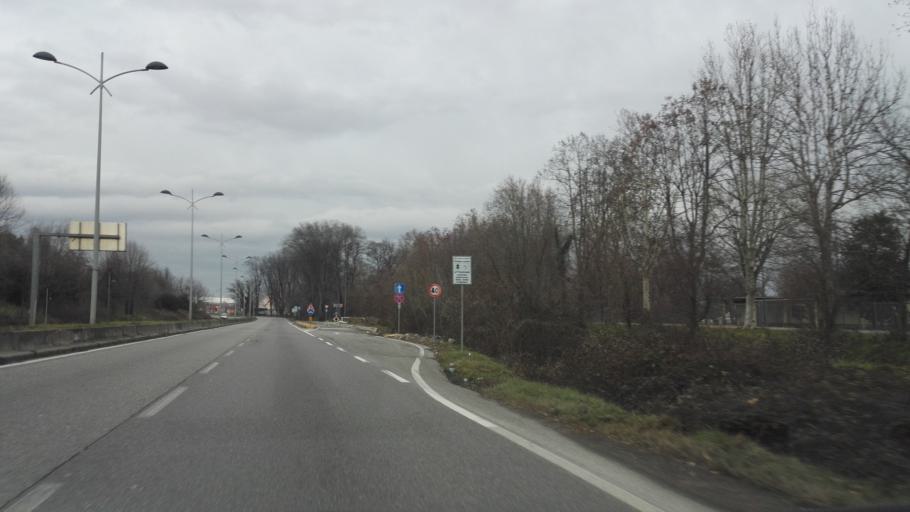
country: IT
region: Lombardy
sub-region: Citta metropolitana di Milano
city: Novegro-Tregarezzo-San Felice
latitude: 45.4672
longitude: 9.2853
